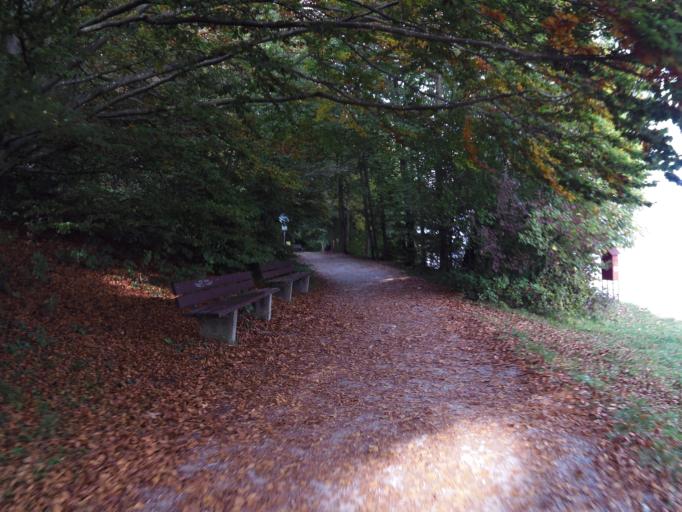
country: DE
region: Bavaria
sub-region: Upper Bavaria
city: Feldafing
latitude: 47.9519
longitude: 11.3100
